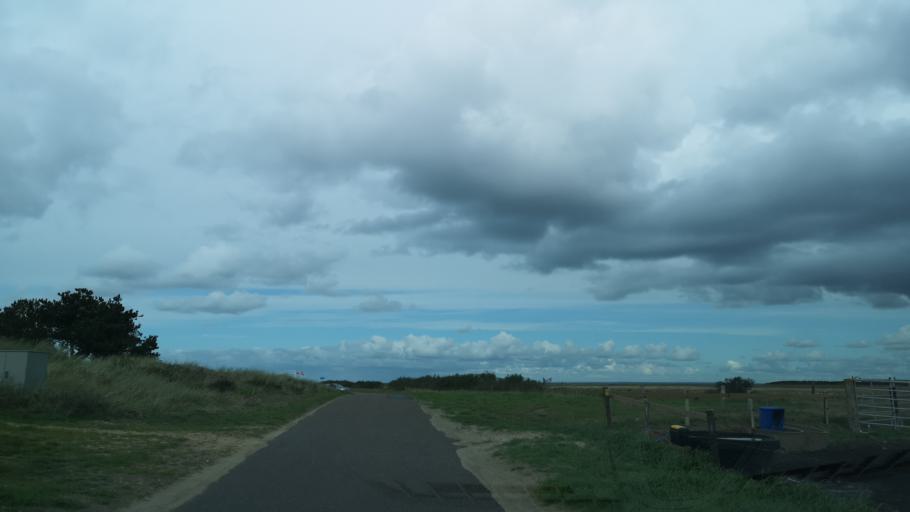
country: DK
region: Central Jutland
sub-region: Ringkobing-Skjern Kommune
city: Hvide Sande
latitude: 55.8514
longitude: 8.2187
